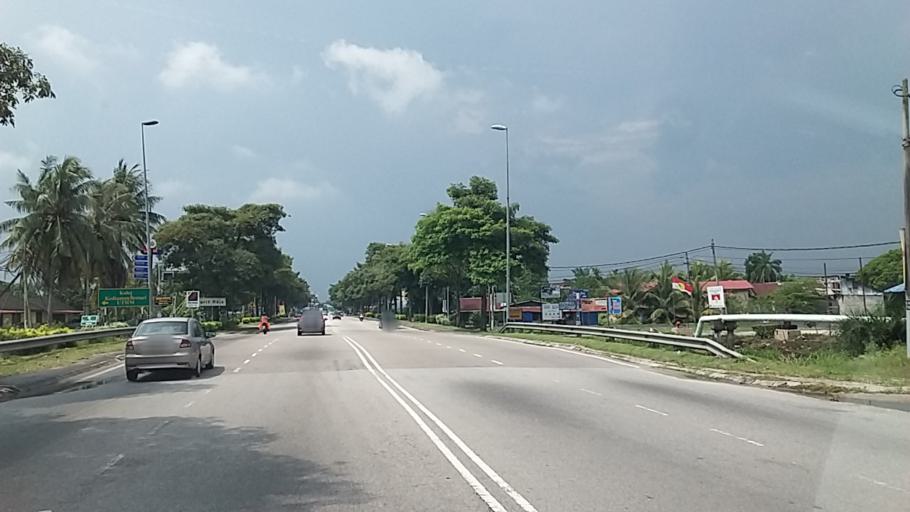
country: MY
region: Johor
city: Parit Raja
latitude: 1.8620
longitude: 103.1064
